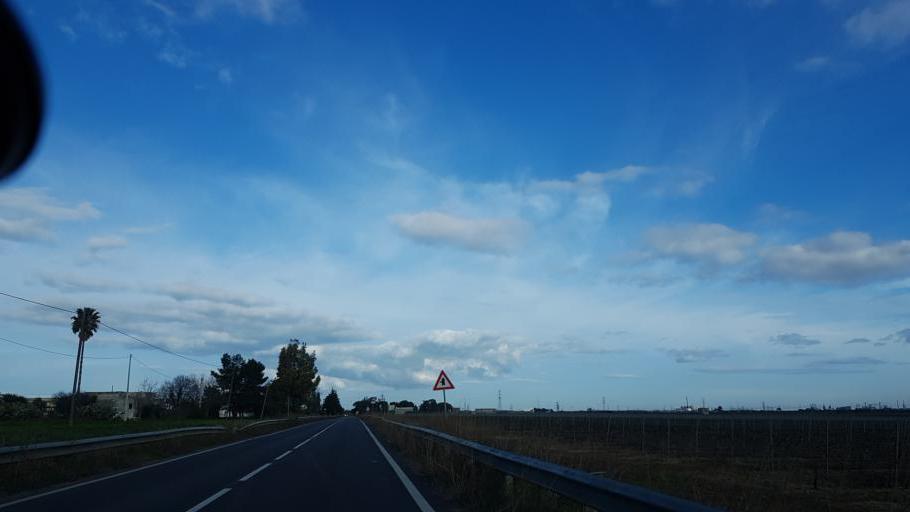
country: IT
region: Apulia
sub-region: Provincia di Brindisi
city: La Rosa
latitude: 40.5781
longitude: 17.9655
